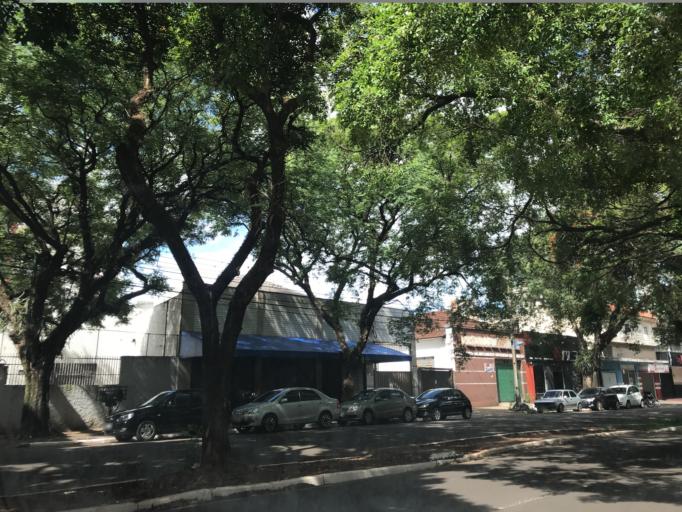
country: BR
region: Parana
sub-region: Maringa
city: Maringa
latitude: -23.4171
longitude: -51.9307
